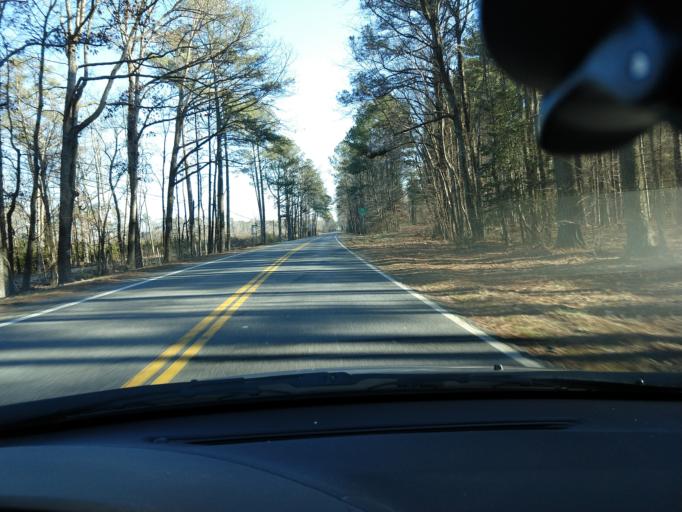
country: US
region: Virginia
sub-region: Charles City County
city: Charles City
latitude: 37.3262
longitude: -76.9840
